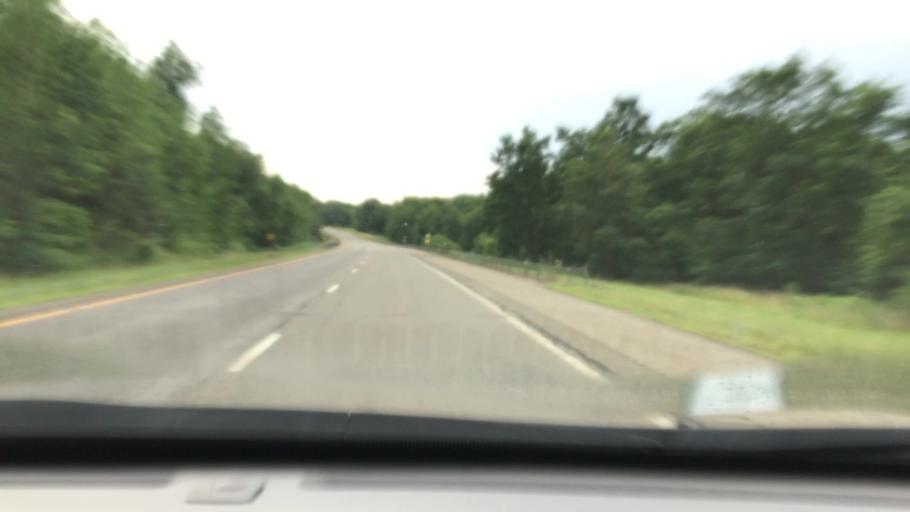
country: US
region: New York
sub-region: Erie County
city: North Boston
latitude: 42.6548
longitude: -78.7657
